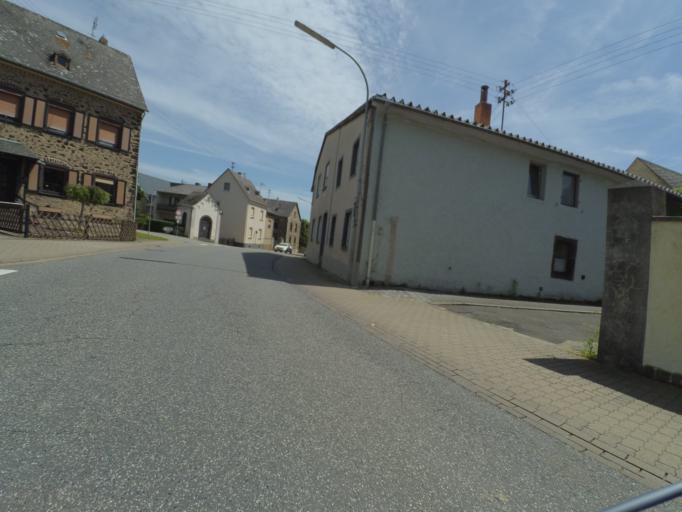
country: DE
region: Rheinland-Pfalz
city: Lonnig
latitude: 50.3112
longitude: 7.4029
